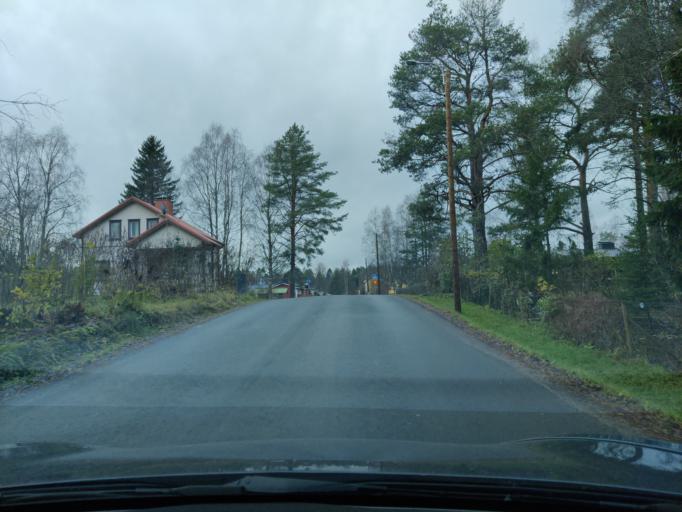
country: FI
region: Northern Savo
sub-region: Ylae-Savo
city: Kiuruvesi
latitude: 63.6475
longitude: 26.6342
